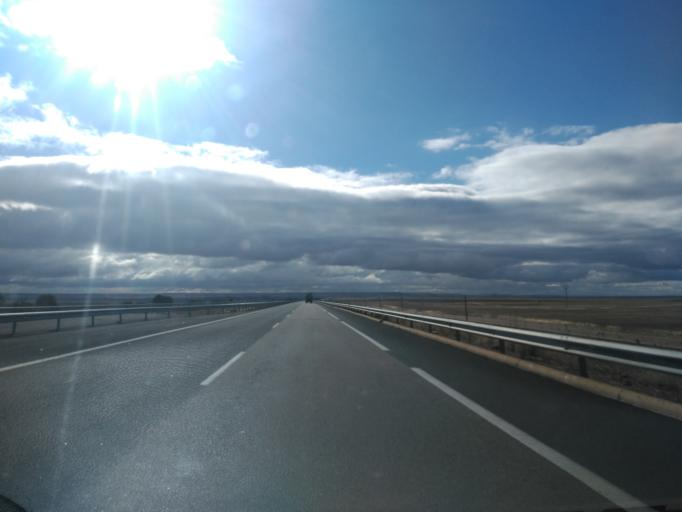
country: ES
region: Castille and Leon
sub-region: Provincia de Palencia
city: Marcilla de Campos
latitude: 42.3027
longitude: -4.3988
